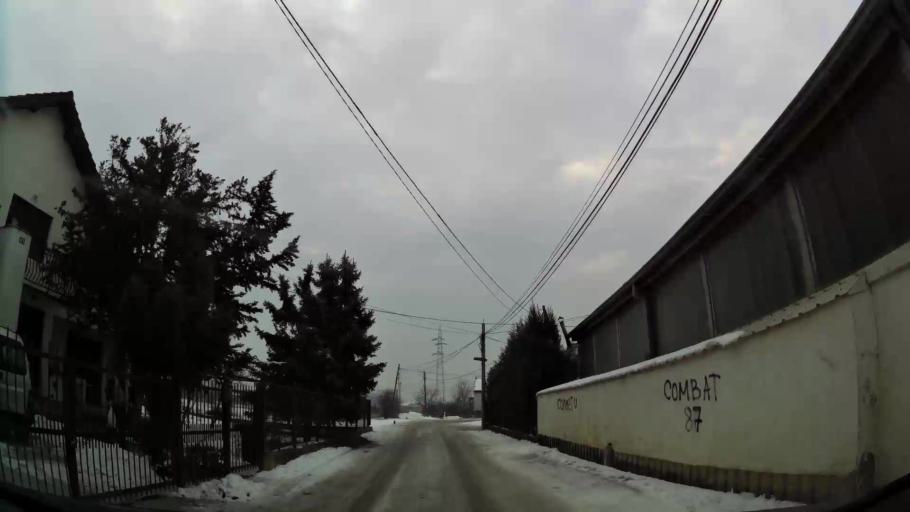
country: MK
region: Saraj
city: Saraj
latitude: 42.0406
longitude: 21.3512
